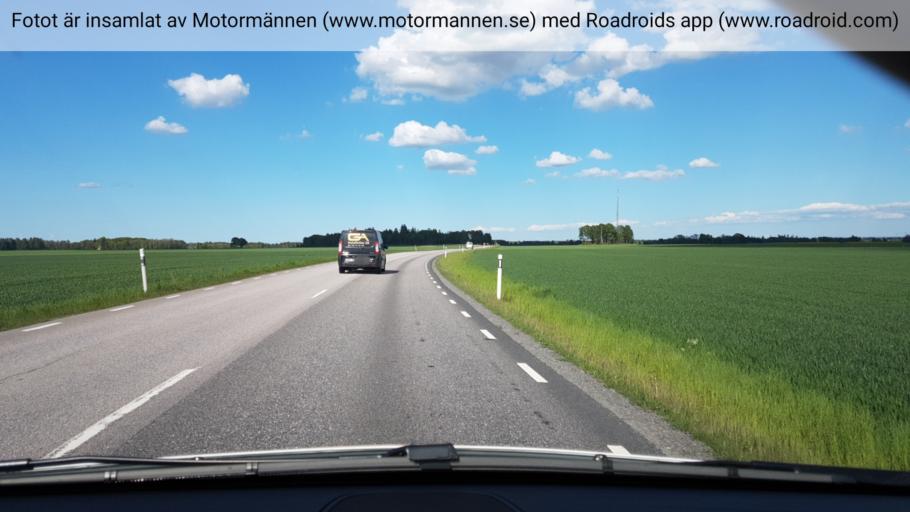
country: SE
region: Vaestra Goetaland
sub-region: Vara Kommun
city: Vara
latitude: 58.3947
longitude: 13.0042
